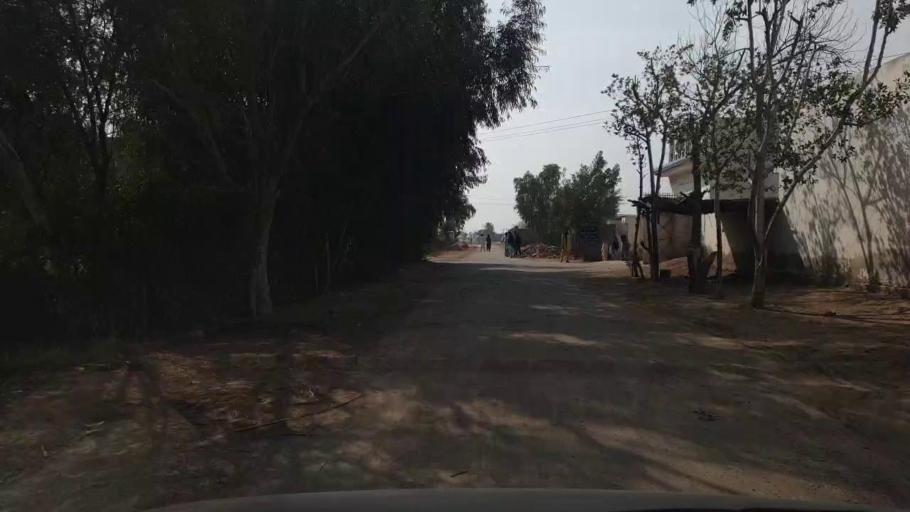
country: PK
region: Sindh
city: Hala
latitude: 25.9851
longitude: 68.4226
